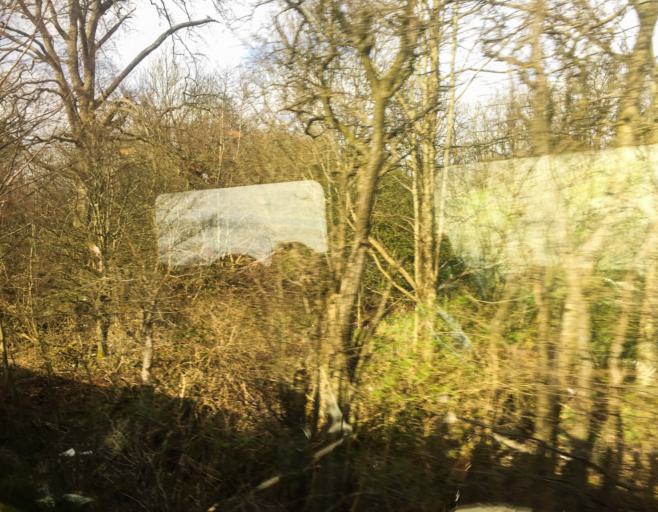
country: GB
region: Scotland
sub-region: East Dunbartonshire
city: Bearsden
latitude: 55.8960
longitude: -4.3200
